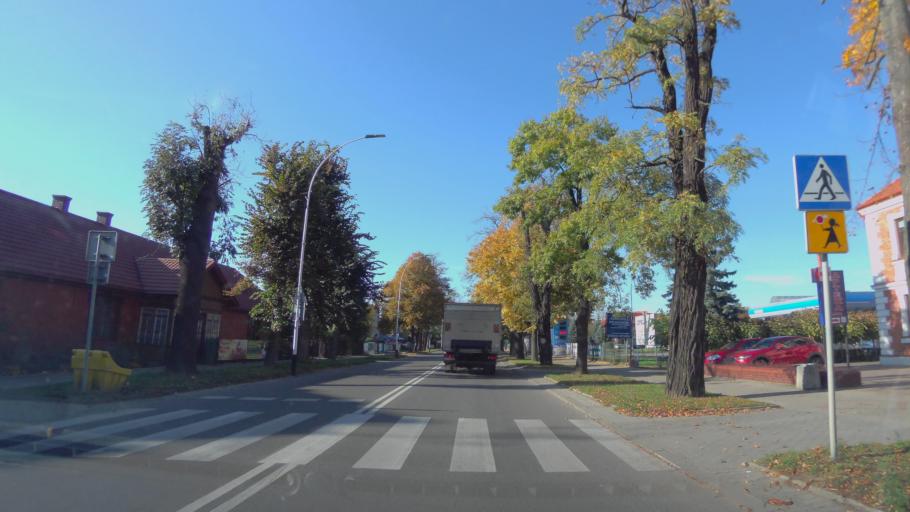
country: PL
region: Subcarpathian Voivodeship
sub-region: Powiat lezajski
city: Lezajsk
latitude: 50.2633
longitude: 22.4178
